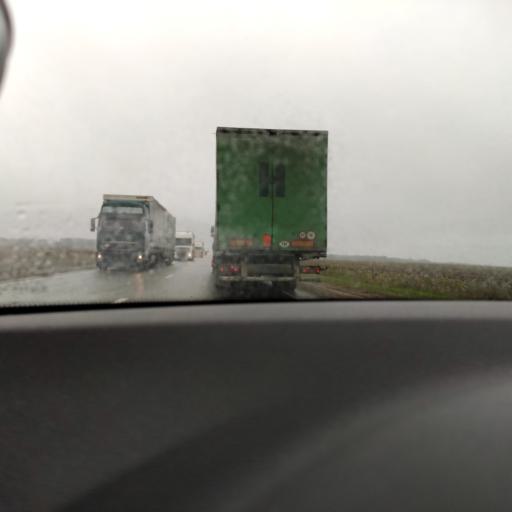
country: RU
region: Samara
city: Yelkhovka
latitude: 53.7140
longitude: 50.2303
